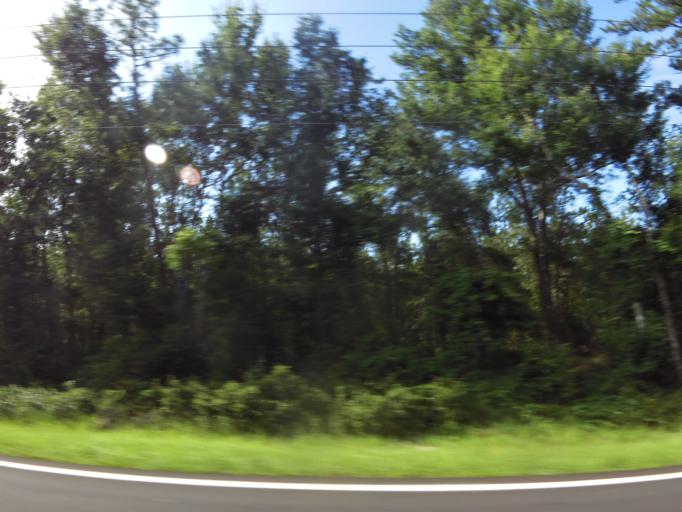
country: US
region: Florida
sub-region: Clay County
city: Green Cove Springs
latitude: 30.0150
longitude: -81.5704
